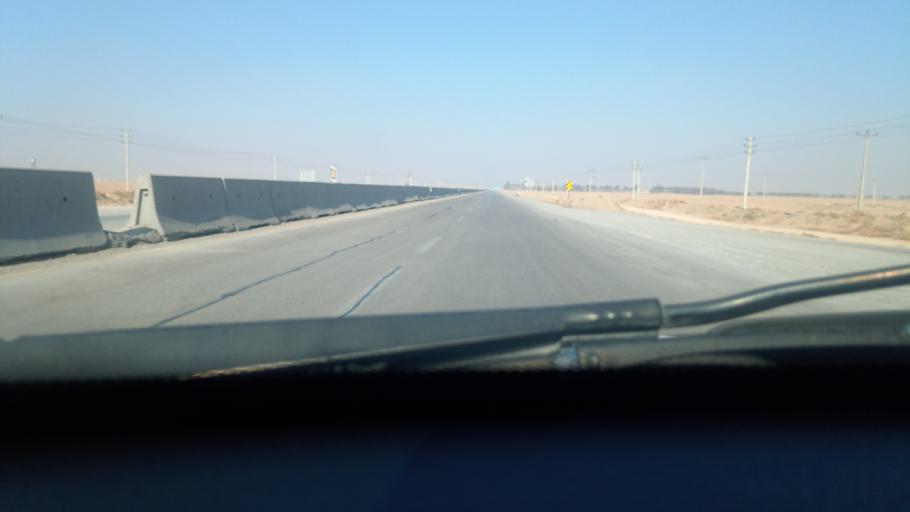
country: IR
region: Razavi Khorasan
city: Quchan
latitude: 36.8995
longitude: 58.7250
